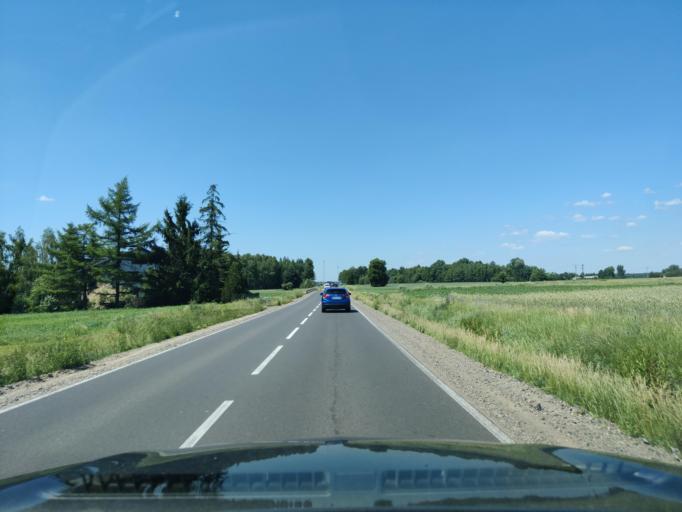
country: PL
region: Masovian Voivodeship
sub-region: Powiat plonski
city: Baboszewo
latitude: 52.7109
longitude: 20.3366
